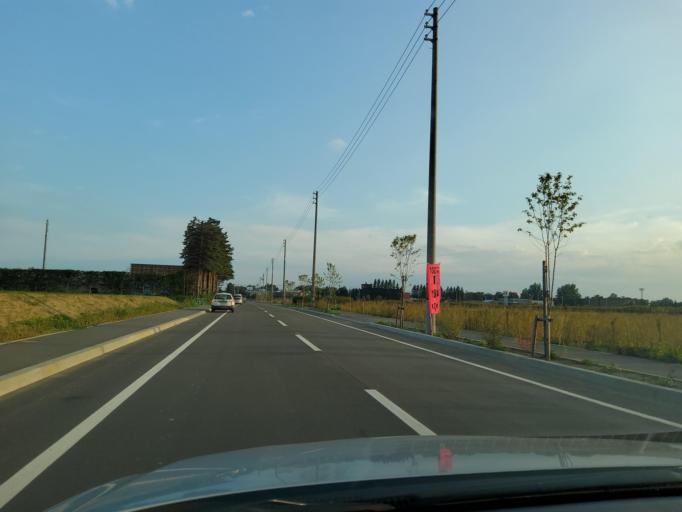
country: JP
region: Hokkaido
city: Obihiro
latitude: 42.9369
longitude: 143.1532
